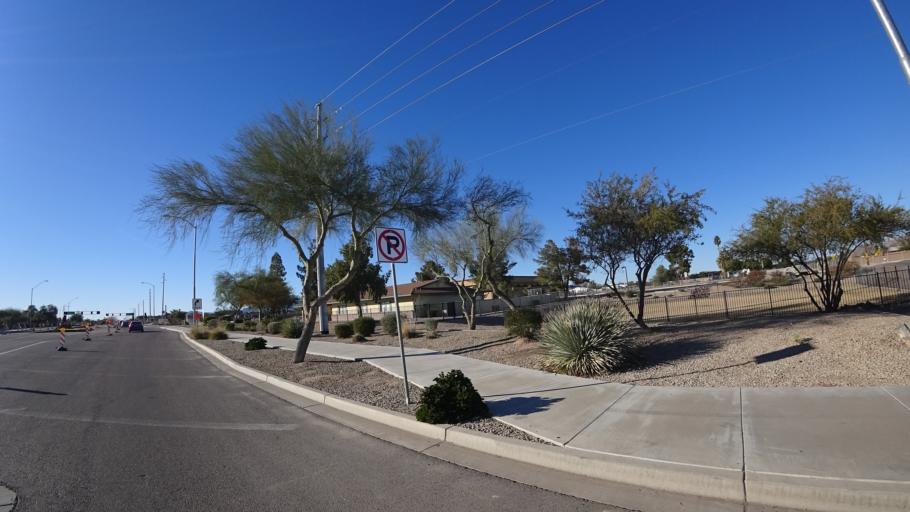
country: US
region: Arizona
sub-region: Maricopa County
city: Goodyear
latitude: 33.4501
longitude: -112.4070
